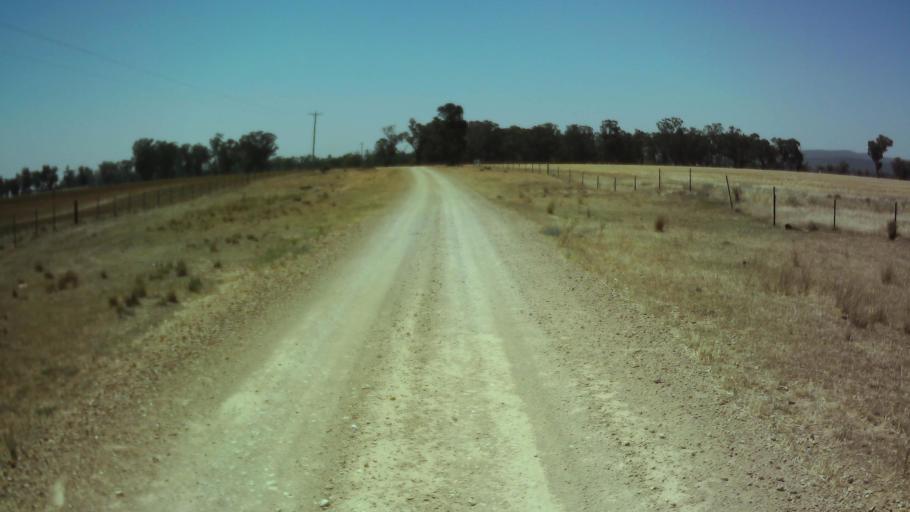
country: AU
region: New South Wales
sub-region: Weddin
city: Grenfell
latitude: -34.0231
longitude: 147.9007
